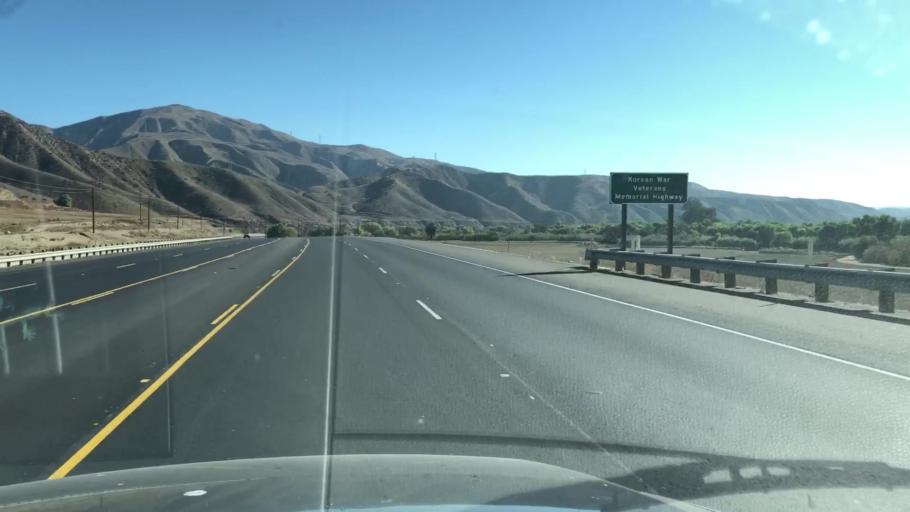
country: US
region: California
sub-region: Ventura County
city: Piru
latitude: 34.4069
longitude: -118.7379
